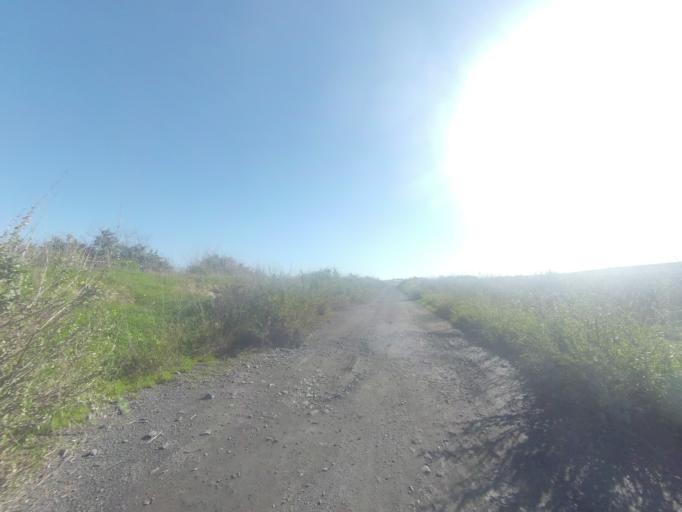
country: ES
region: Andalusia
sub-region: Provincia de Huelva
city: Palos de la Frontera
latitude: 37.2544
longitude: -6.9088
